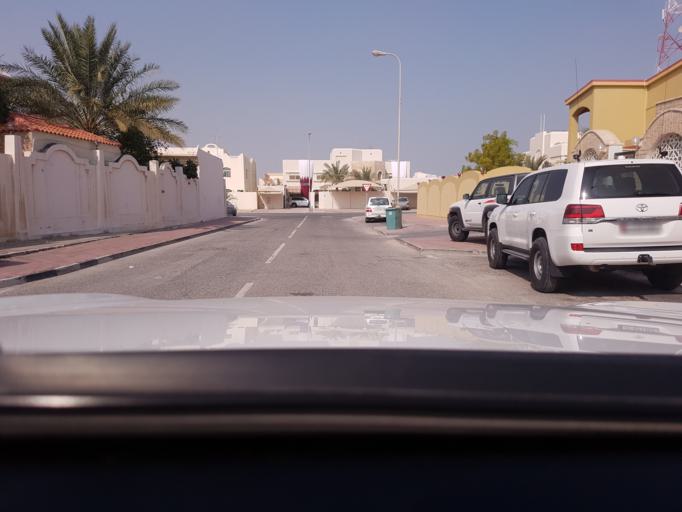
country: QA
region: Baladiyat ad Dawhah
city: Doha
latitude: 25.2360
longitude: 51.5589
